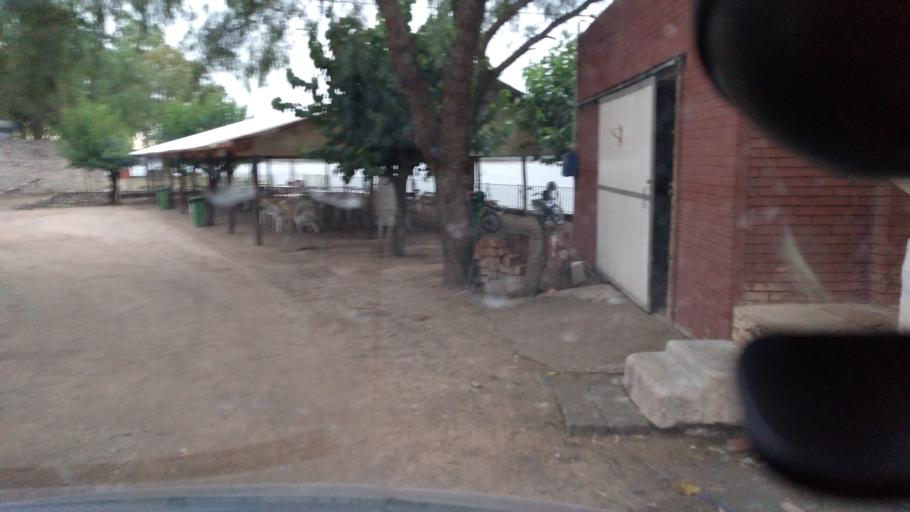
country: AR
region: Cordoba
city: Villa Las Rosas
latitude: -31.8776
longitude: -65.0226
